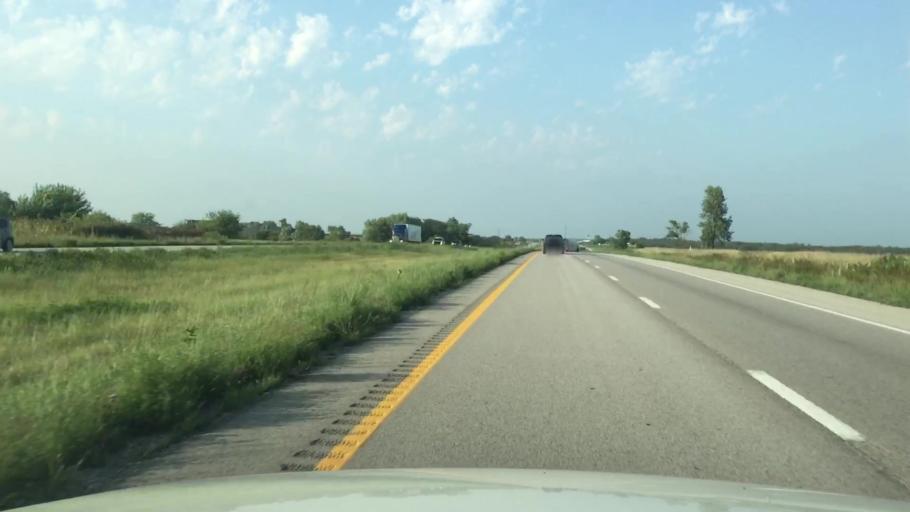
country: US
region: Missouri
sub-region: Clinton County
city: Cameron
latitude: 39.8340
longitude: -94.1853
